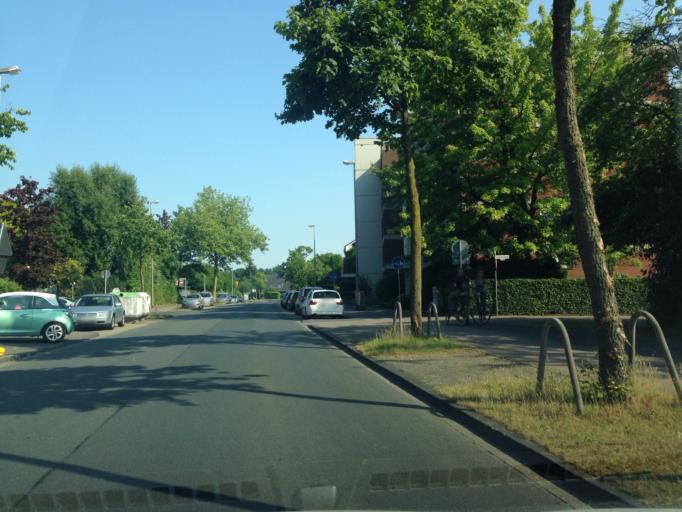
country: DE
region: North Rhine-Westphalia
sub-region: Regierungsbezirk Munster
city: Muenster
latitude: 51.9669
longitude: 7.5809
